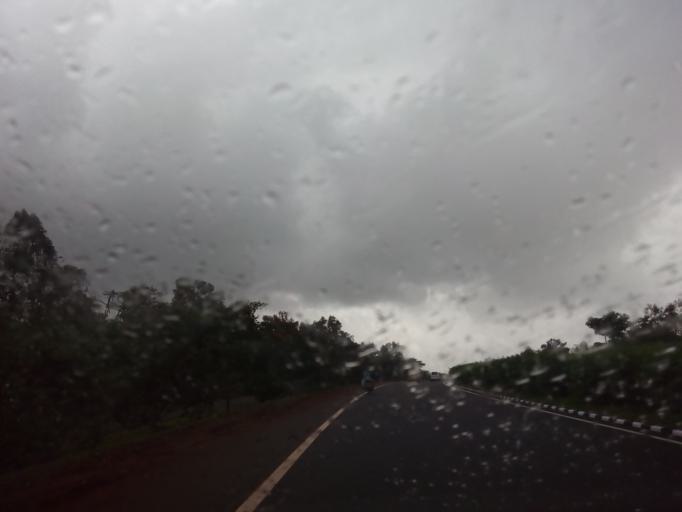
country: IN
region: Karnataka
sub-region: Belgaum
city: Belgaum
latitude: 16.0115
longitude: 74.5160
